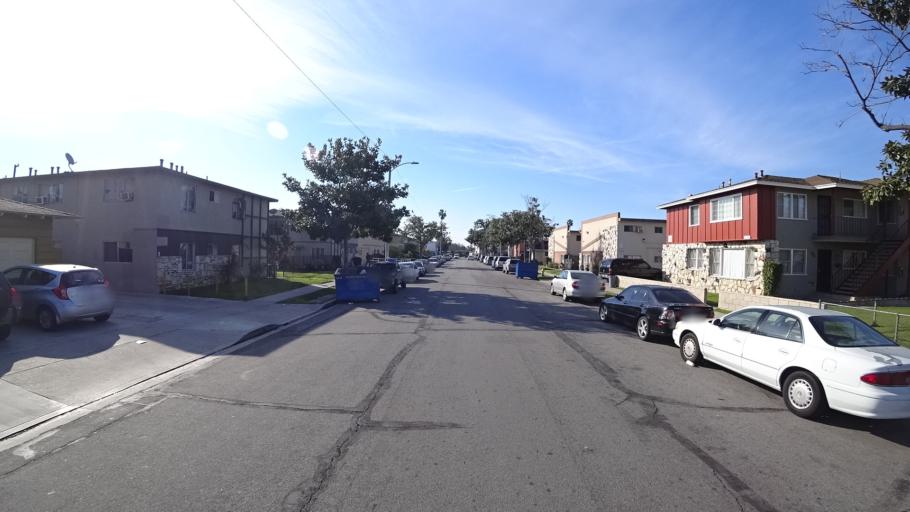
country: US
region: California
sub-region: Orange County
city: Anaheim
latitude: 33.8489
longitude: -117.9299
